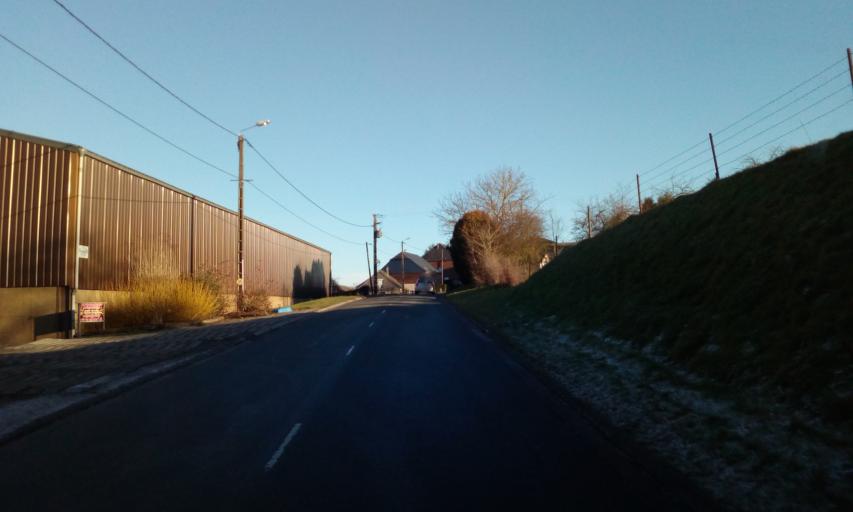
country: FR
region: Picardie
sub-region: Departement de l'Aisne
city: Rozoy-sur-Serre
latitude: 49.7071
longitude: 4.1482
